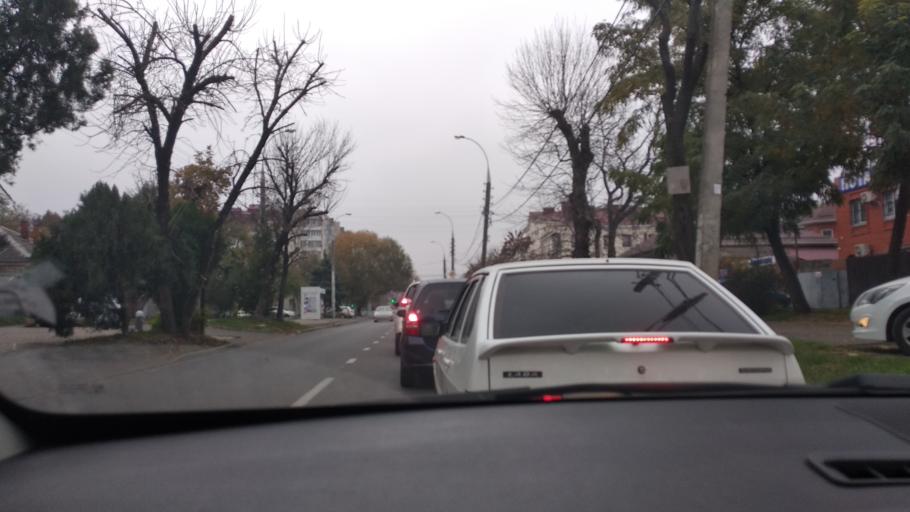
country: RU
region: Krasnodarskiy
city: Krasnodar
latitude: 45.0221
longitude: 39.0097
